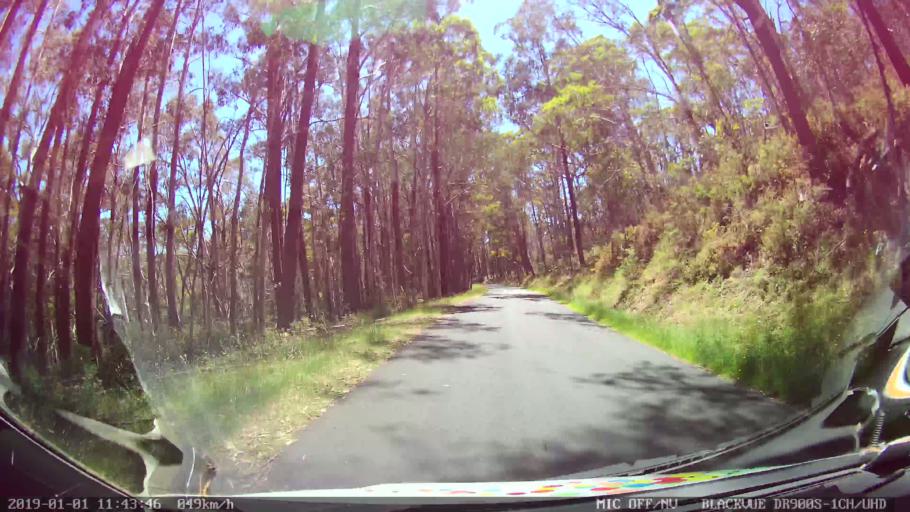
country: AU
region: New South Wales
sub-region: Snowy River
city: Jindabyne
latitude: -35.9039
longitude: 148.3883
